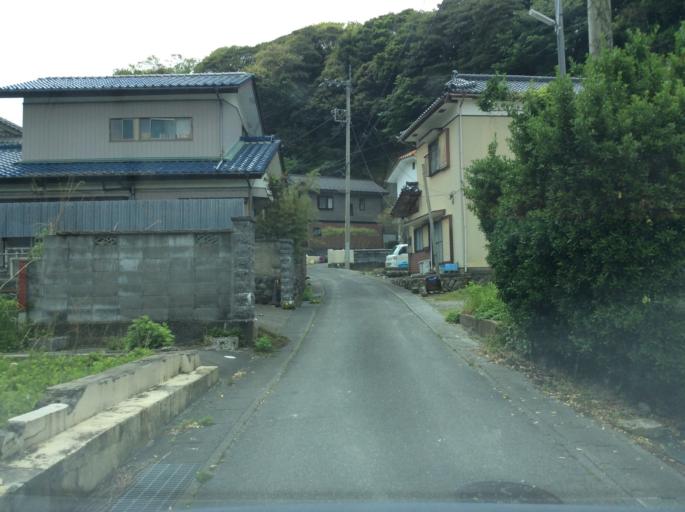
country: JP
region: Ibaraki
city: Kitaibaraki
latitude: 36.8549
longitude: 140.7943
